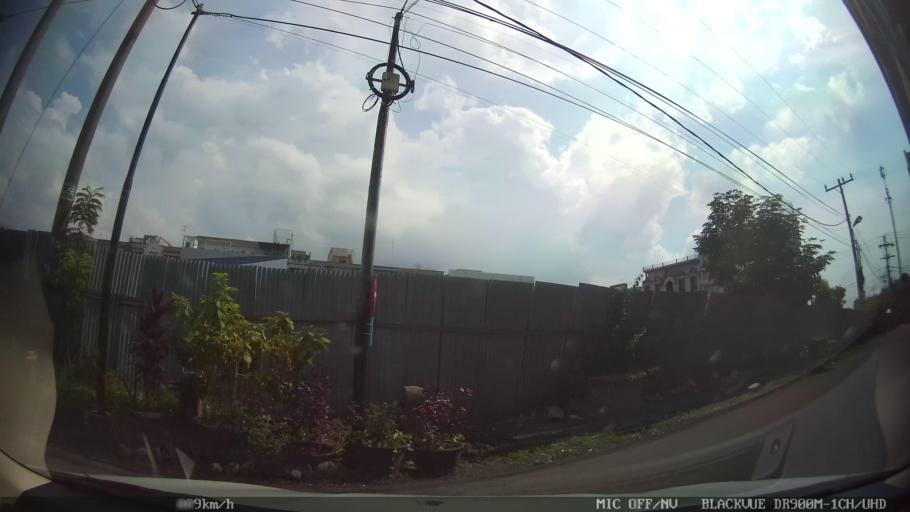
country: ID
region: North Sumatra
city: Medan
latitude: 3.5901
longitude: 98.6623
